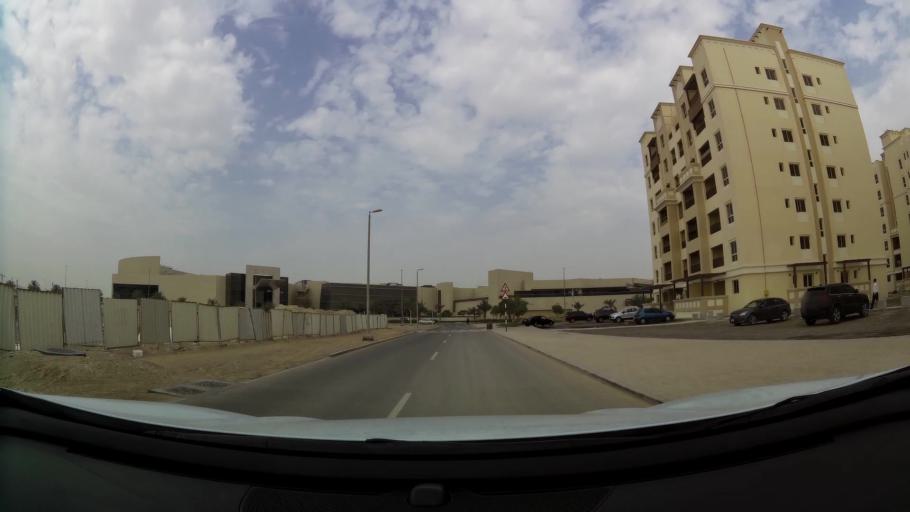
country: AE
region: Abu Dhabi
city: Abu Dhabi
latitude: 24.3104
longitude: 54.6226
